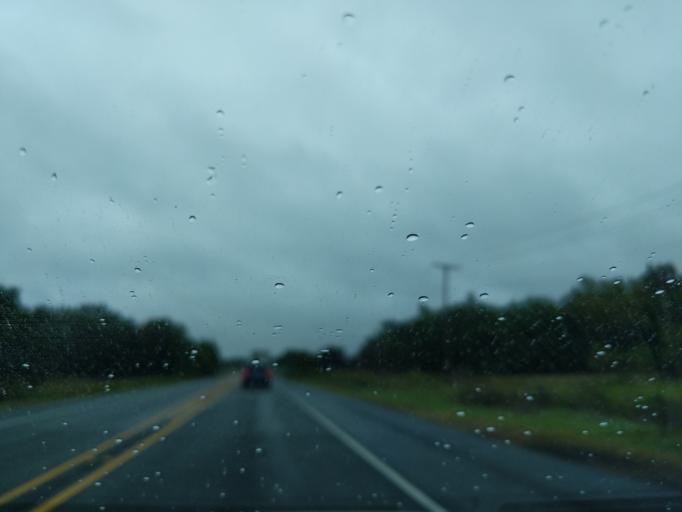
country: US
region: Louisiana
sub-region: Caddo Parish
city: Greenwood
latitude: 32.4408
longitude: -93.9823
